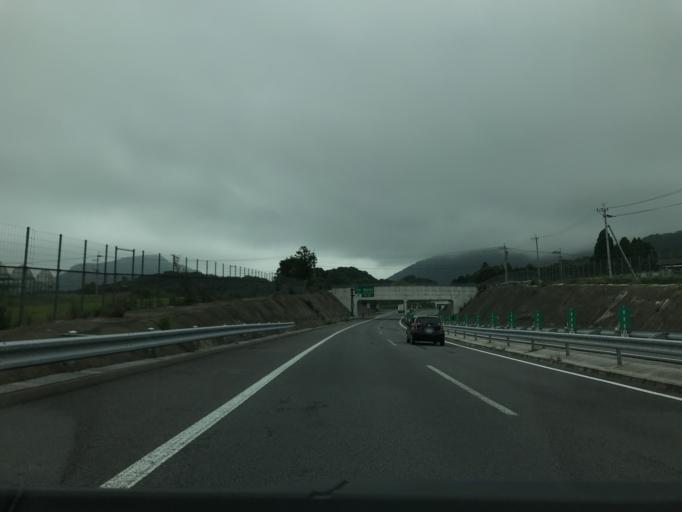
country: JP
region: Oita
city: Bungo-Takada-shi
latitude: 33.5015
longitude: 131.3142
